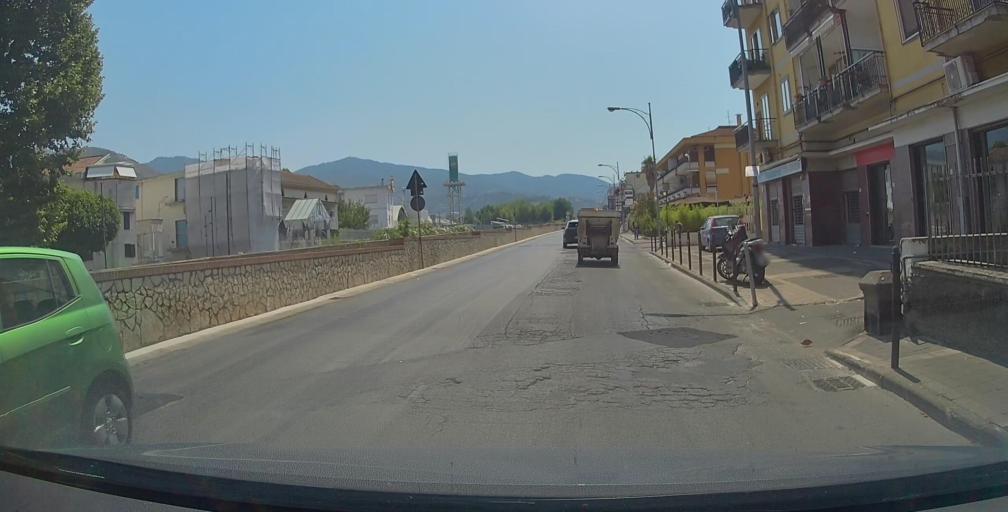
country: IT
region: Campania
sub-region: Provincia di Salerno
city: Nocera Superiore
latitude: 40.7395
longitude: 14.6719
